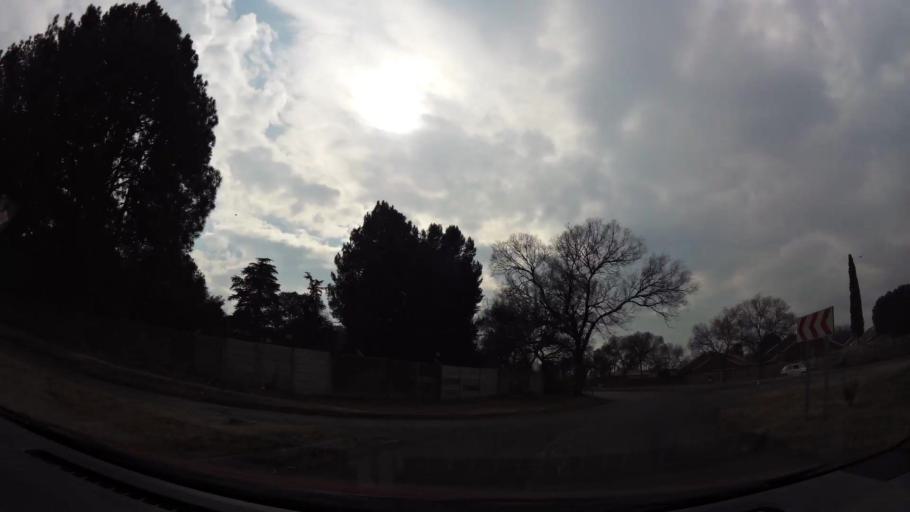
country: ZA
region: Gauteng
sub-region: Sedibeng District Municipality
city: Vanderbijlpark
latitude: -26.6884
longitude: 27.8254
